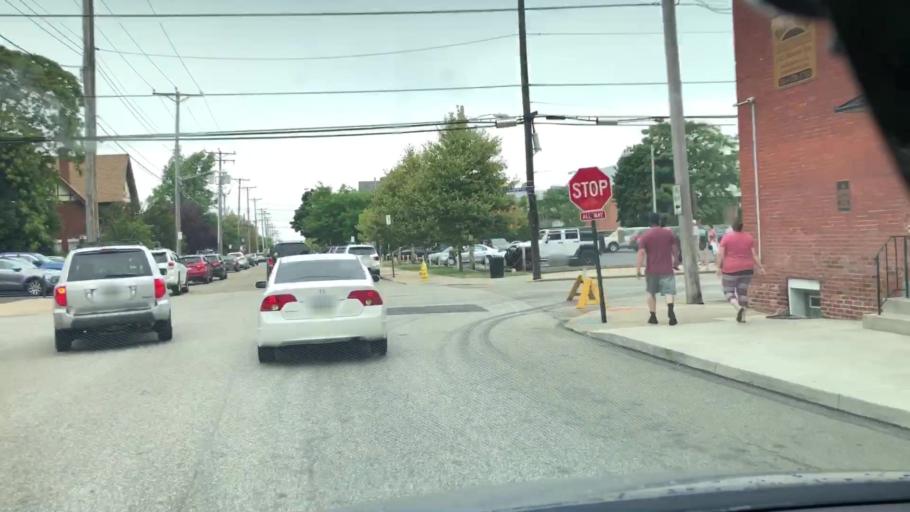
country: US
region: Pennsylvania
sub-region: Erie County
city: Erie
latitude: 42.1298
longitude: -80.0872
